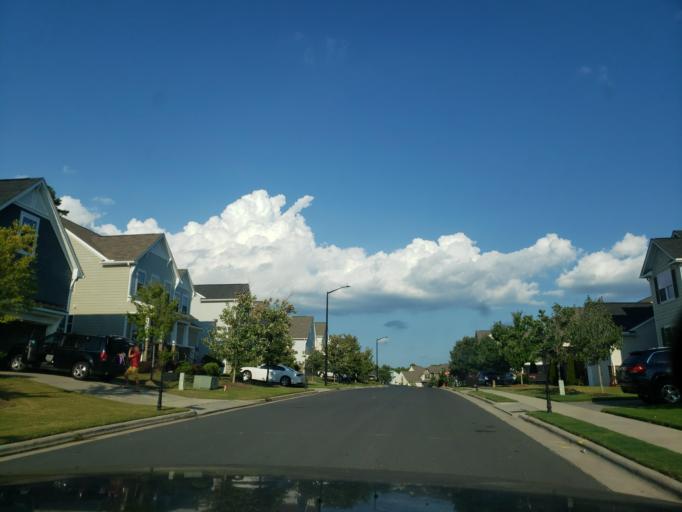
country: US
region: North Carolina
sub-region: Durham County
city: Durham
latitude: 35.9324
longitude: -78.9320
